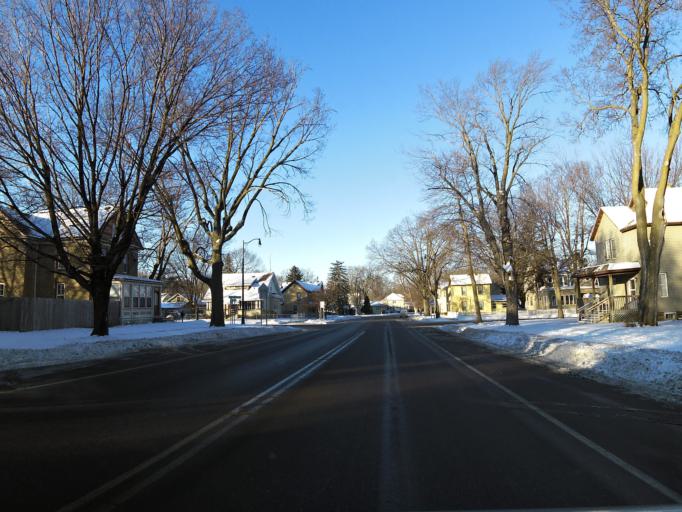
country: US
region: Minnesota
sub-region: Scott County
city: Jordan
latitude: 44.6674
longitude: -93.6283
